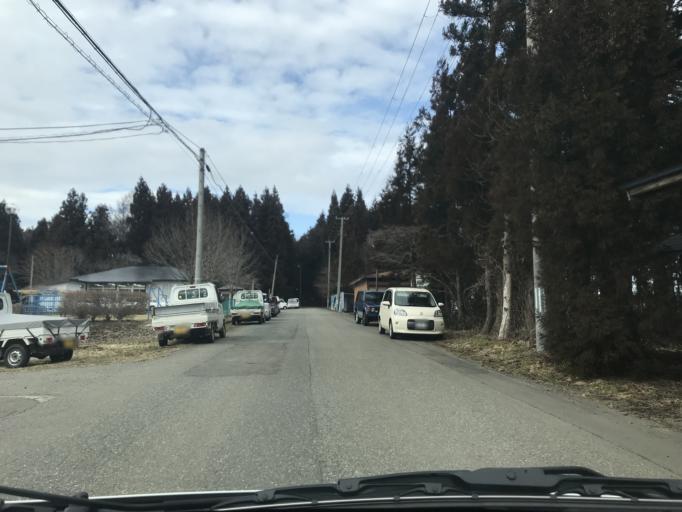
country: JP
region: Iwate
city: Kitakami
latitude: 39.3328
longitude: 140.9842
